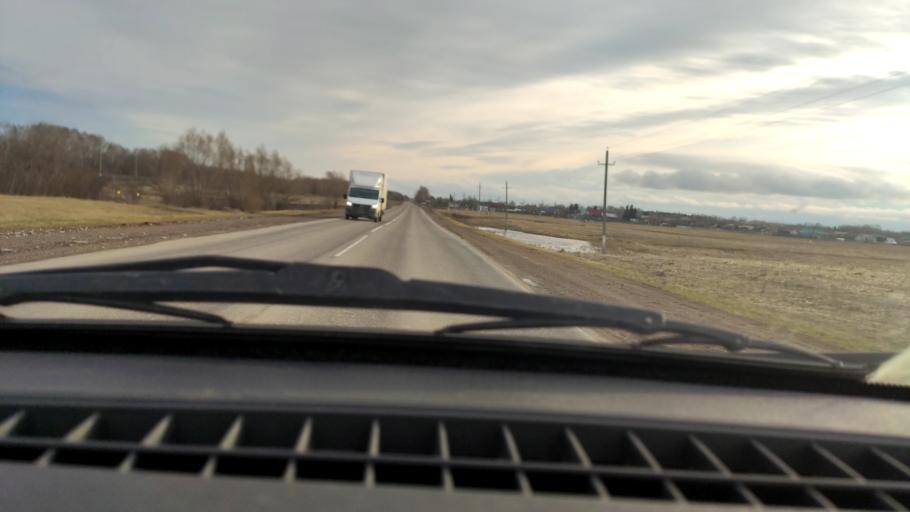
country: RU
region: Bashkortostan
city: Davlekanovo
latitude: 54.3037
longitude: 55.1357
